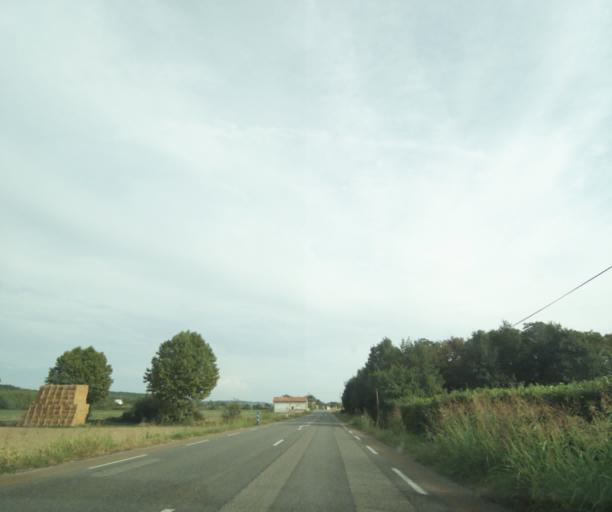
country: FR
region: Midi-Pyrenees
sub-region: Departement du Tarn-et-Garonne
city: Verdun-sur-Garonne
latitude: 43.8697
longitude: 1.2646
